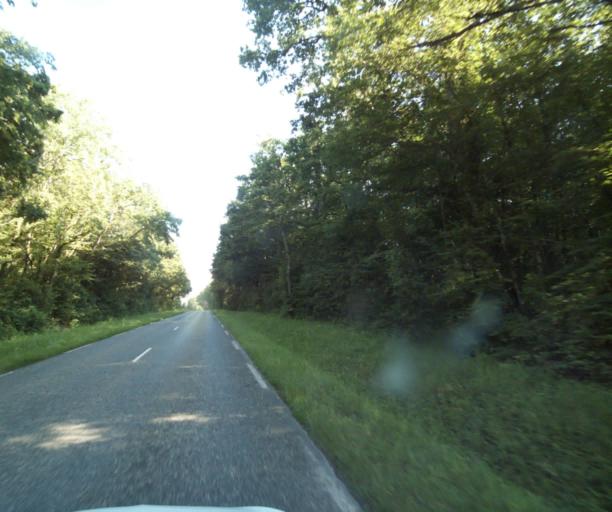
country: FR
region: Rhone-Alpes
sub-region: Departement de la Haute-Savoie
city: Messery
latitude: 46.3388
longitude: 6.2918
